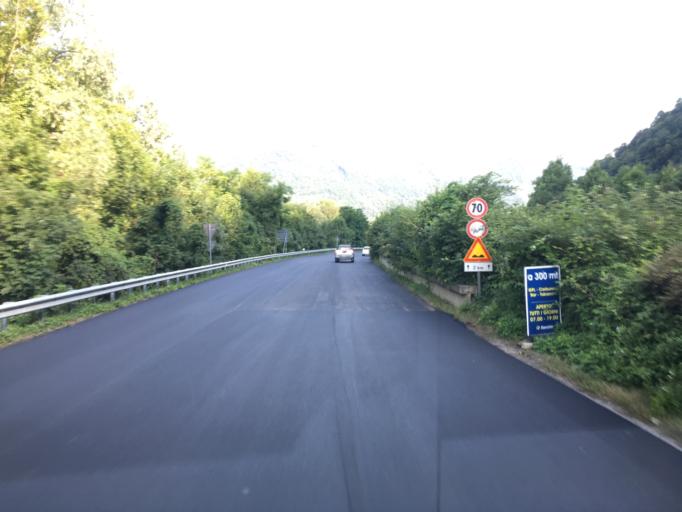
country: IT
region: Piedmont
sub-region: Provincia di Torino
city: Villar Perosa
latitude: 44.9195
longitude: 7.2397
